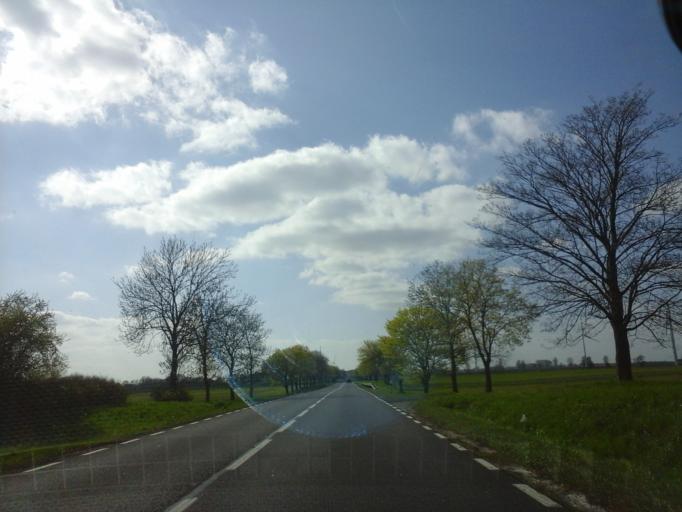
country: PL
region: West Pomeranian Voivodeship
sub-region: Powiat stargardzki
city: Suchan
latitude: 53.2816
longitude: 15.2967
